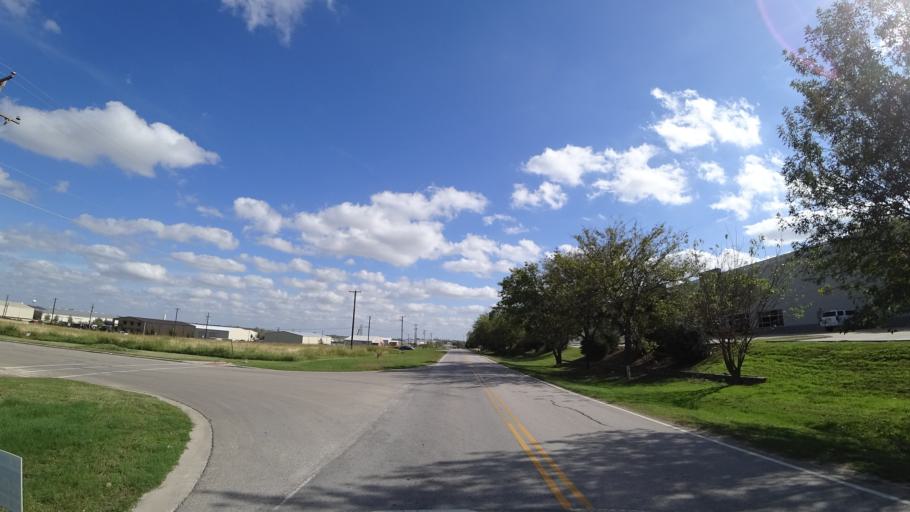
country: US
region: Texas
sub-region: Travis County
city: Windemere
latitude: 30.4684
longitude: -97.6661
